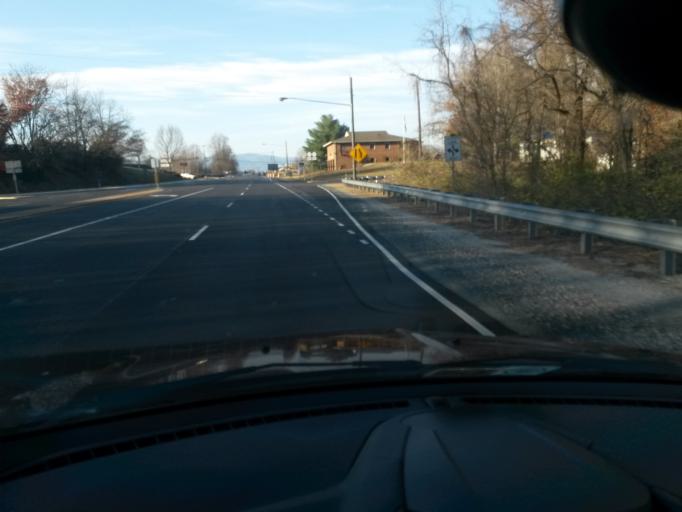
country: US
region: Virginia
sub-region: Amherst County
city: Amherst
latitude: 37.5835
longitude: -79.0467
